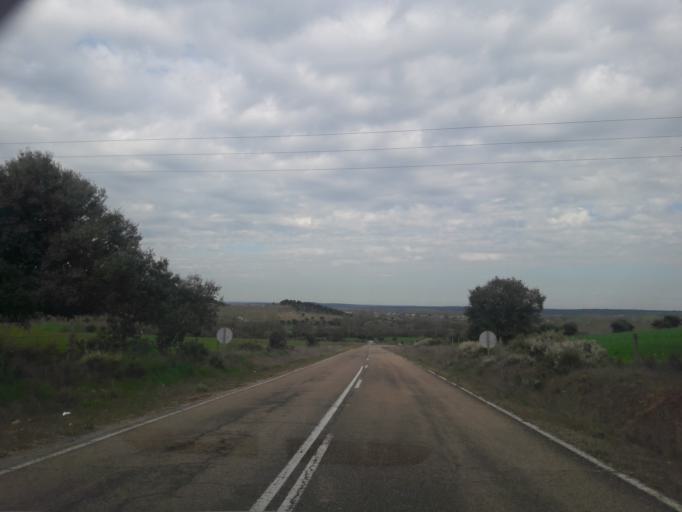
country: ES
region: Castille and Leon
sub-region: Provincia de Salamanca
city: Ciudad Rodrigo
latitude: 40.5765
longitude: -6.5341
